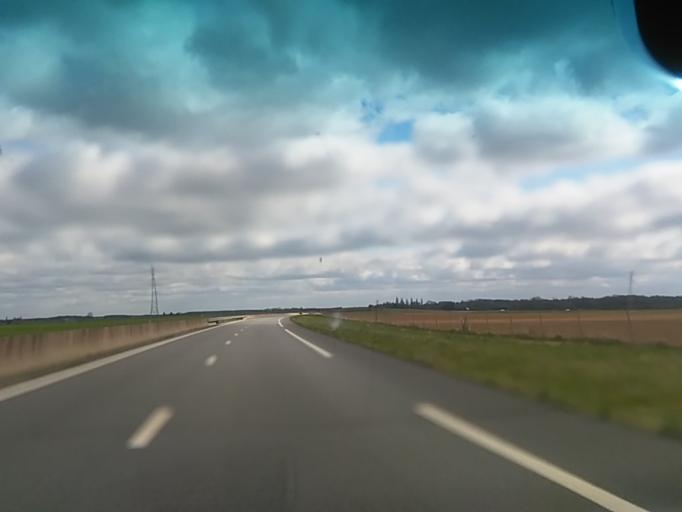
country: FR
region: Haute-Normandie
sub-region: Departement de l'Eure
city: Brionne
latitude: 49.1648
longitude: 0.6726
